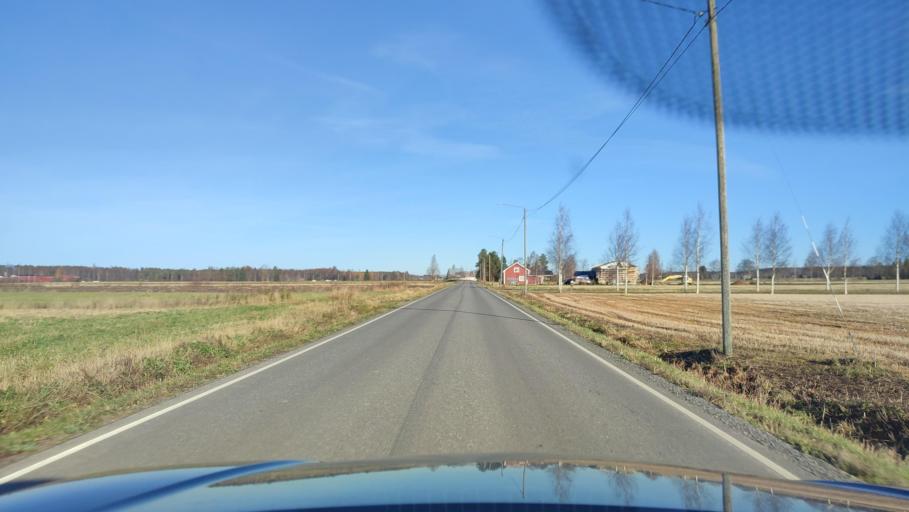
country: FI
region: Southern Ostrobothnia
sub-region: Suupohja
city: Karijoki
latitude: 62.2939
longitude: 21.7192
